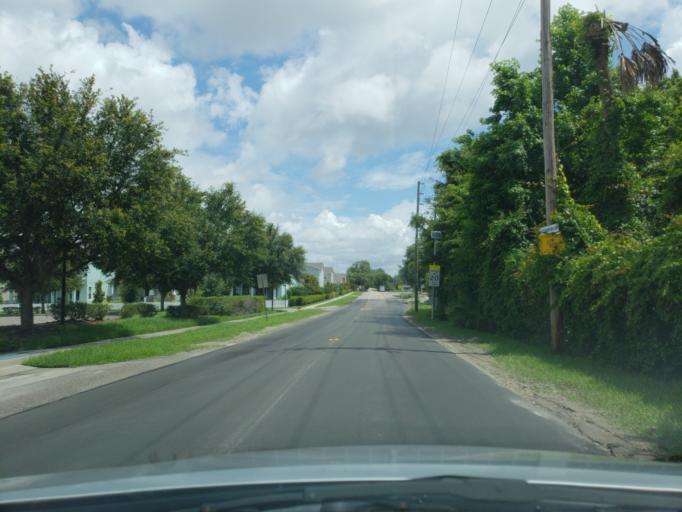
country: US
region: Florida
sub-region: Hillsborough County
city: Riverview
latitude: 27.8870
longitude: -82.3103
